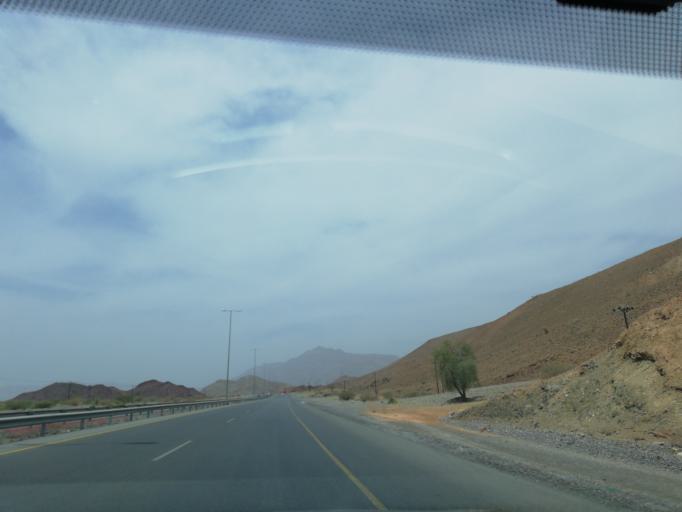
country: OM
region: Muhafazat ad Dakhiliyah
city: Izki
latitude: 22.8831
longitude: 57.7027
